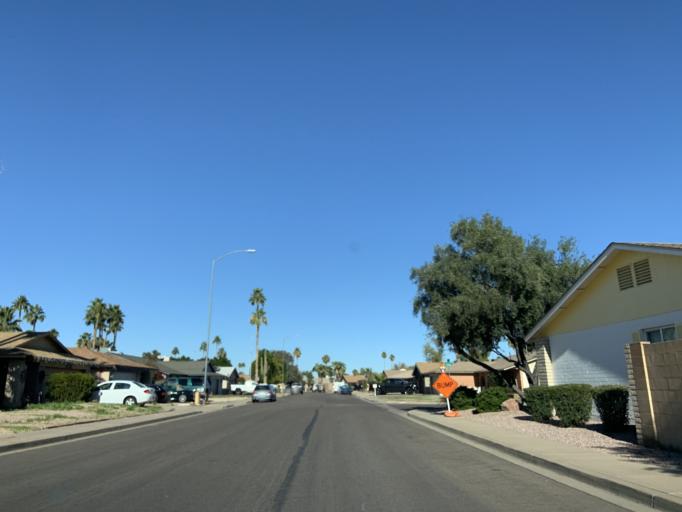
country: US
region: Arizona
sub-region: Maricopa County
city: San Carlos
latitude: 33.3578
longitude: -111.8565
